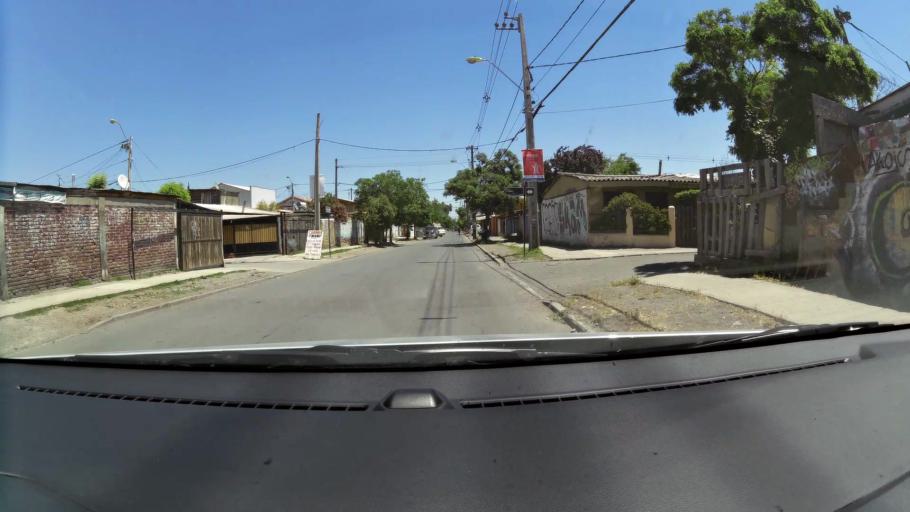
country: CL
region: Santiago Metropolitan
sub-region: Provincia de Santiago
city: La Pintana
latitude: -33.5765
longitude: -70.6679
